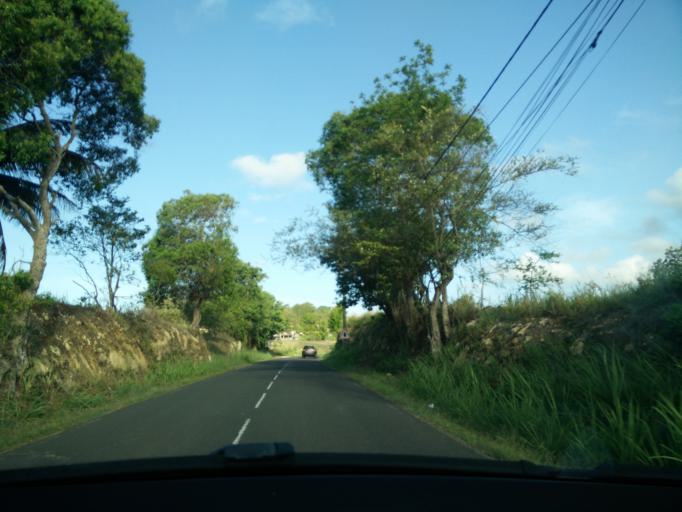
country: GP
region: Guadeloupe
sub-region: Guadeloupe
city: Sainte-Anne
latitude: 16.2765
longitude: -61.3895
